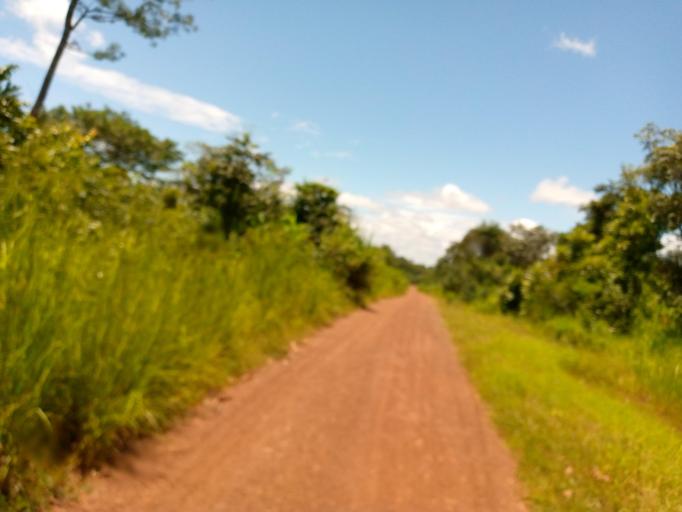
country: SL
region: Northern Province
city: Binkolo
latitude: 9.1157
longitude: -12.1349
